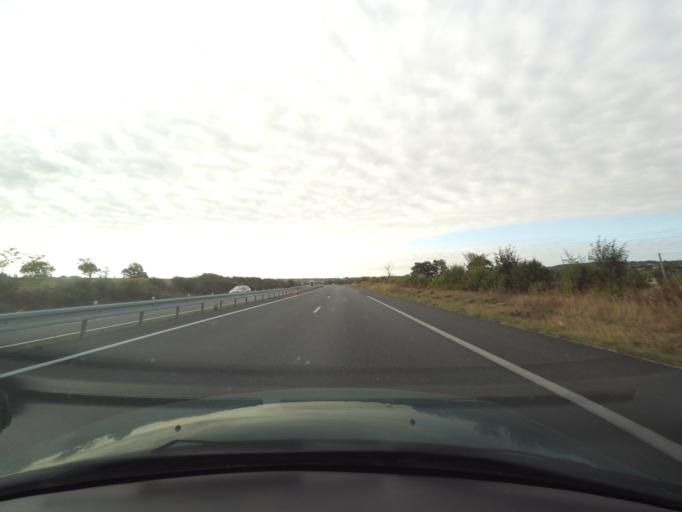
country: FR
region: Poitou-Charentes
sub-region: Departement des Deux-Sevres
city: Saint-Pierre-des-Echaubrognes
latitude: 46.9665
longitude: -0.7978
